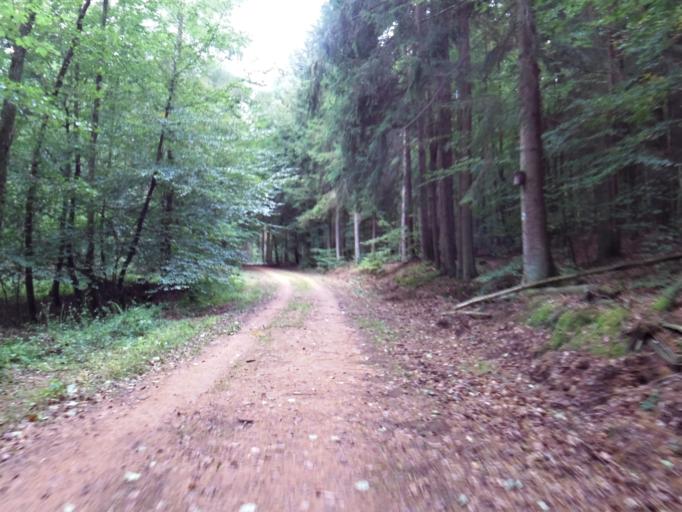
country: DE
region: Rheinland-Pfalz
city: Neuhemsbach
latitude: 49.5054
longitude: 7.9672
